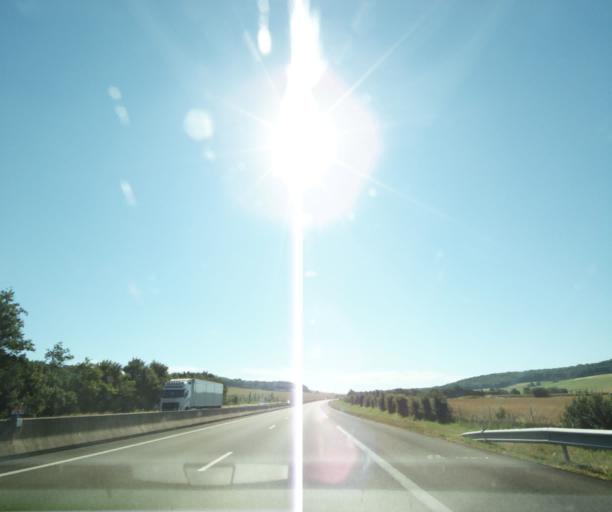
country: FR
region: Champagne-Ardenne
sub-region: Departement de la Haute-Marne
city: Nogent-le-Bas
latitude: 47.9574
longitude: 5.4051
